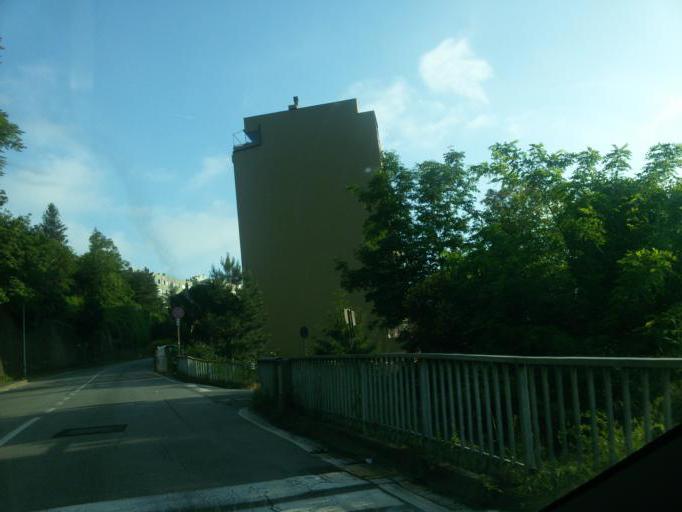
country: IT
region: Liguria
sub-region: Provincia di Genova
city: Genoa
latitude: 44.4521
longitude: 8.9093
